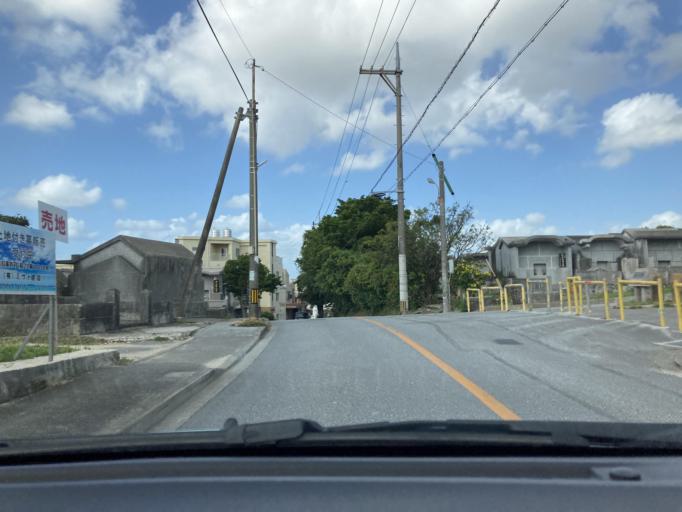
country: JP
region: Okinawa
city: Naha-shi
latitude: 26.2082
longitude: 127.7114
